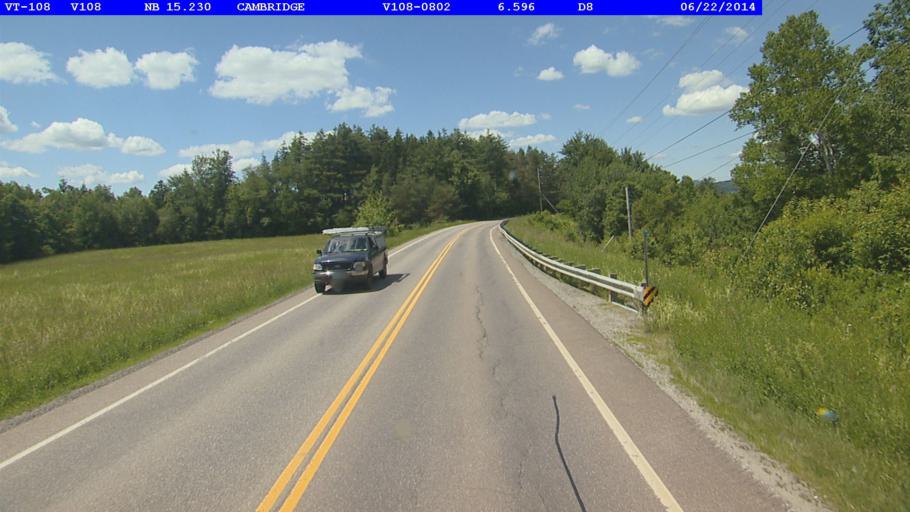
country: US
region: Vermont
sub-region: Lamoille County
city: Johnson
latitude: 44.6171
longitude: -72.8199
